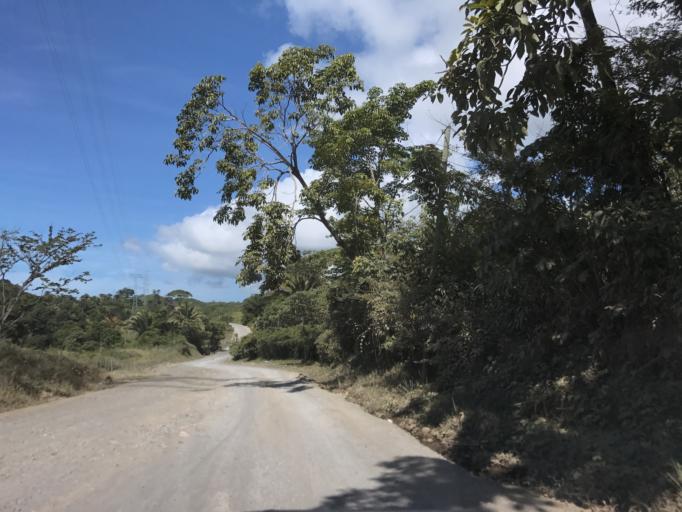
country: GT
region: Izabal
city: Morales
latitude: 15.6375
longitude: -89.0408
